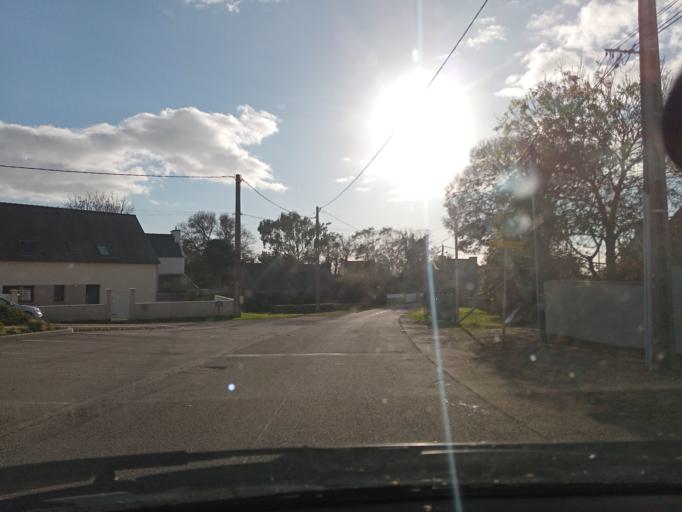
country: FR
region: Brittany
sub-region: Departement du Finistere
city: Audierne
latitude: 48.0193
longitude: -4.5150
